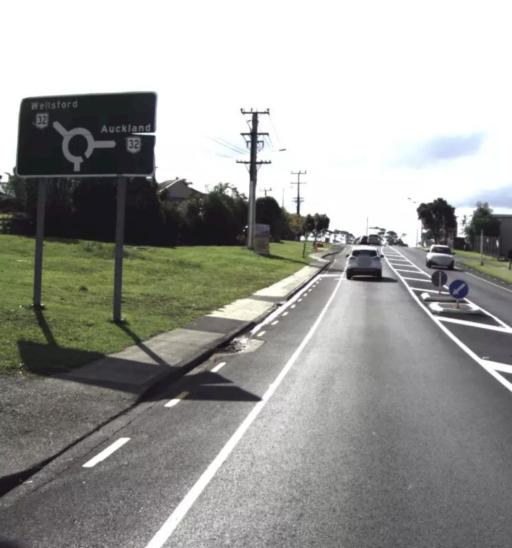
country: NZ
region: Auckland
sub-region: Auckland
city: Rosebank
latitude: -36.8236
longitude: 174.6075
